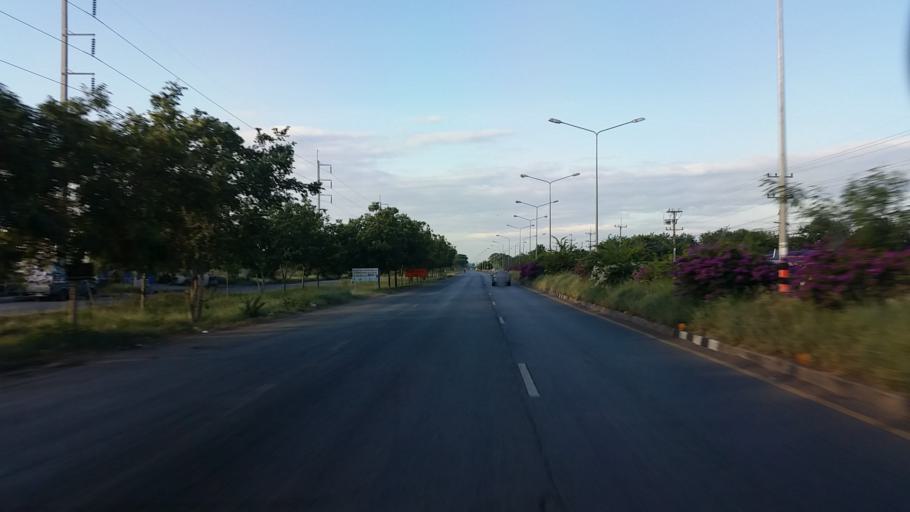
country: TH
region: Lop Buri
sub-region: Amphoe Tha Luang
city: Tha Luang
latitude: 15.0848
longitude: 101.0061
